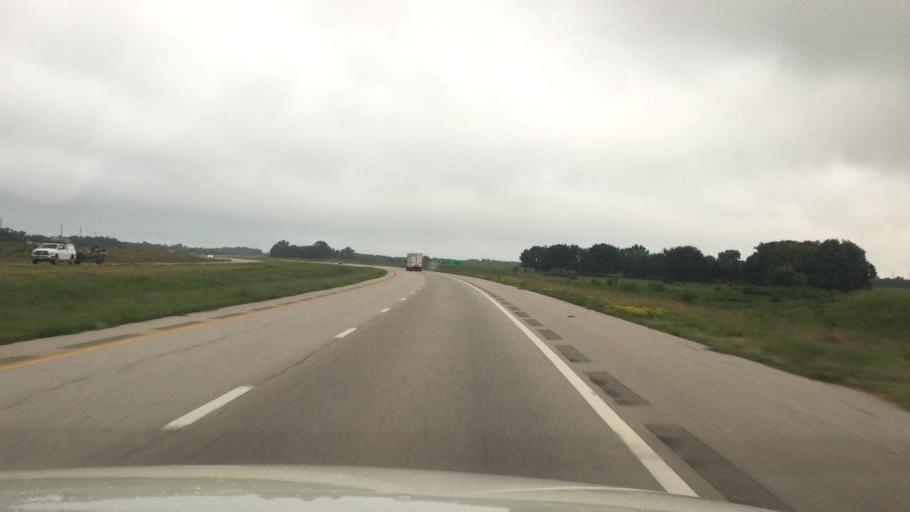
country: US
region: Kansas
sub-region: Montgomery County
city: Coffeyville
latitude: 37.0791
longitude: -95.5898
